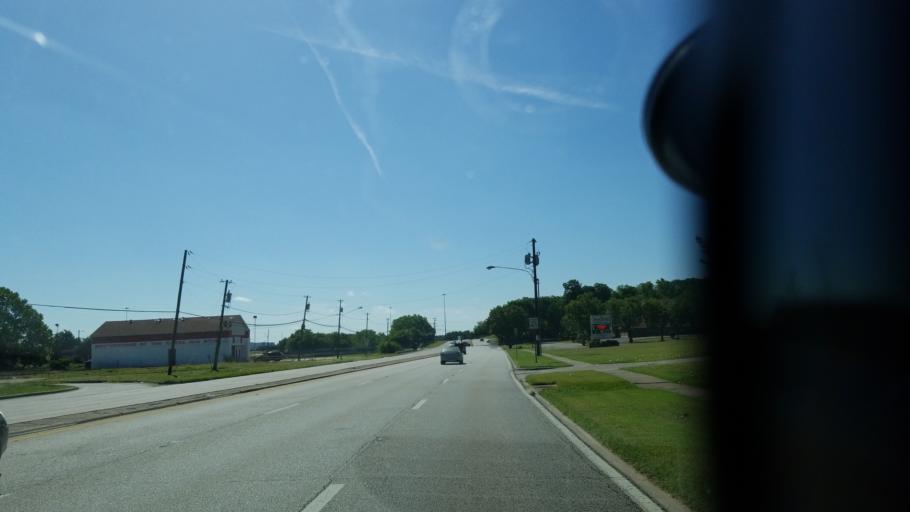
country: US
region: Texas
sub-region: Dallas County
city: Cockrell Hill
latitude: 32.6899
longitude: -96.8313
